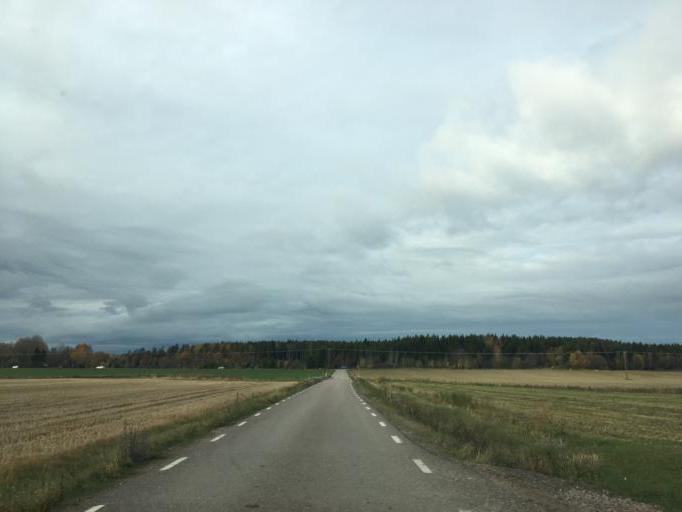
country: SE
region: Vaestmanland
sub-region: Hallstahammars Kommun
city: Kolback
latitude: 59.5502
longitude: 16.3414
